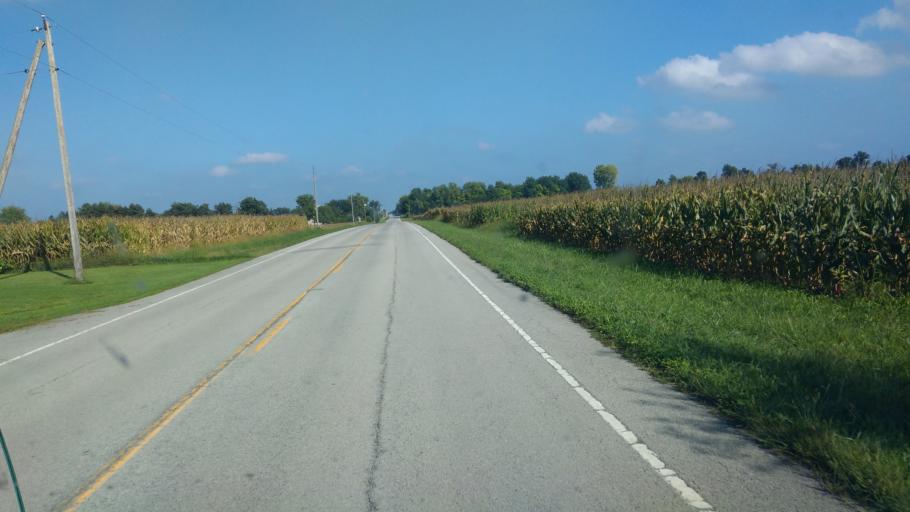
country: US
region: Ohio
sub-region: Hancock County
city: Arlington
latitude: 40.8341
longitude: -83.6800
